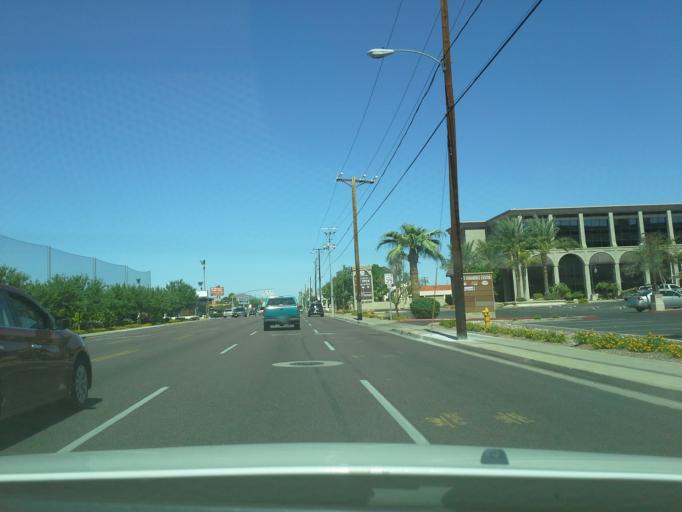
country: US
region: Arizona
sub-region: Maricopa County
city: Phoenix
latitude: 33.5061
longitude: -112.0650
